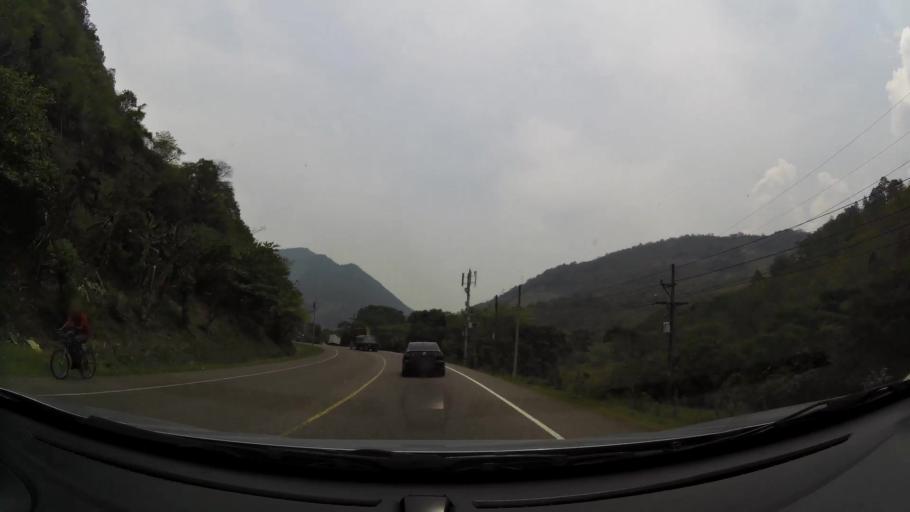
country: HN
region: Comayagua
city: Taulabe
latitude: 14.7291
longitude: -87.9632
